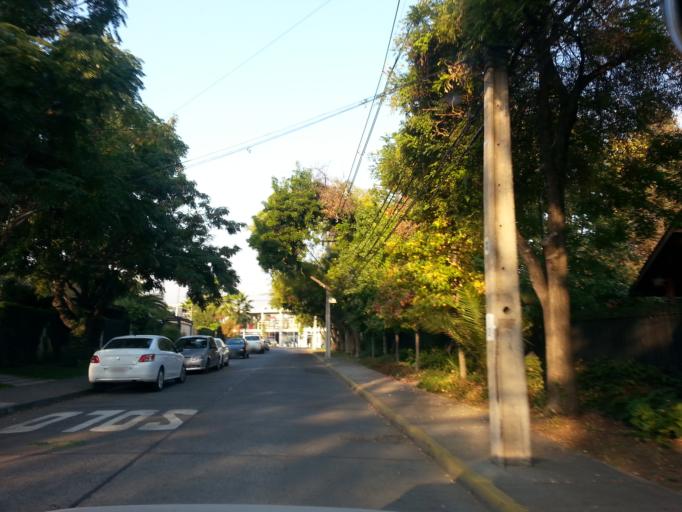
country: CL
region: Santiago Metropolitan
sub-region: Provincia de Santiago
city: Villa Presidente Frei, Nunoa, Santiago, Chile
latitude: -33.3830
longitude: -70.5738
